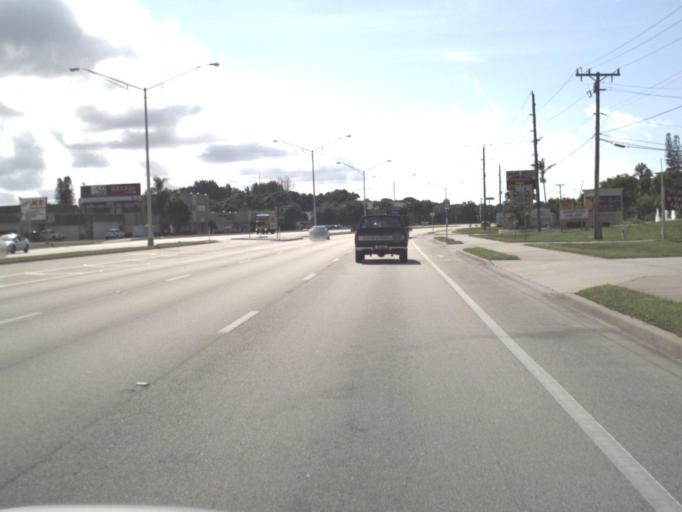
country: US
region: Florida
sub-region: Sarasota County
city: Laurel
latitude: 27.1332
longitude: -82.4550
